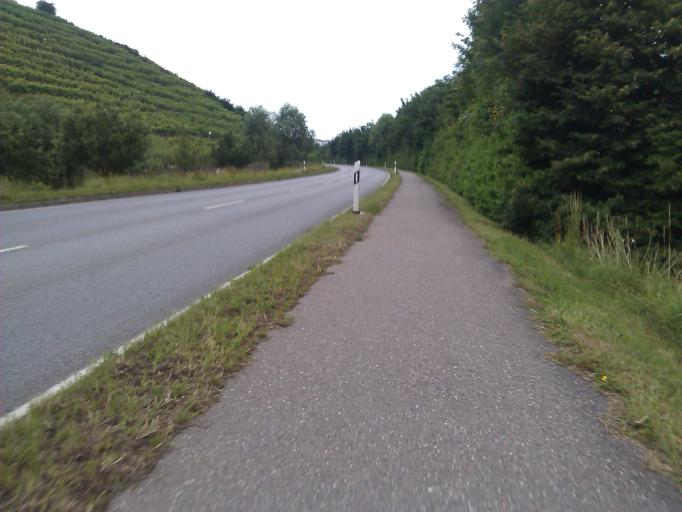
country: DE
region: Baden-Wuerttemberg
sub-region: Regierungsbezirk Stuttgart
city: Lauffen am Neckar
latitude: 49.0667
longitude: 9.1216
